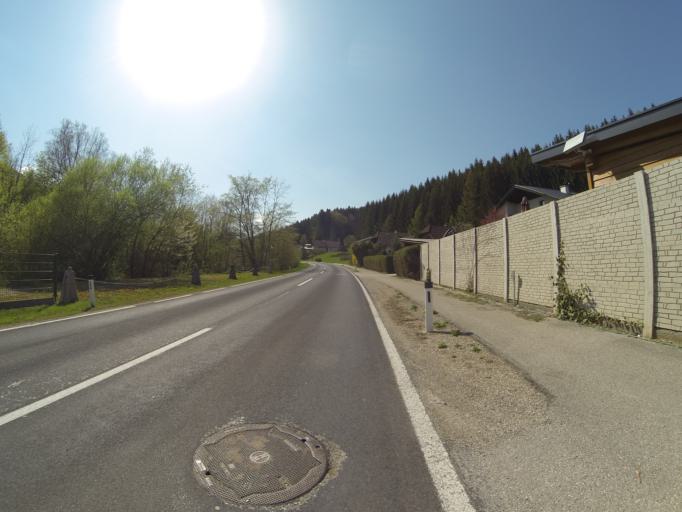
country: AT
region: Upper Austria
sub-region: Politischer Bezirk Gmunden
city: Altmunster
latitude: 47.9218
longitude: 13.7380
